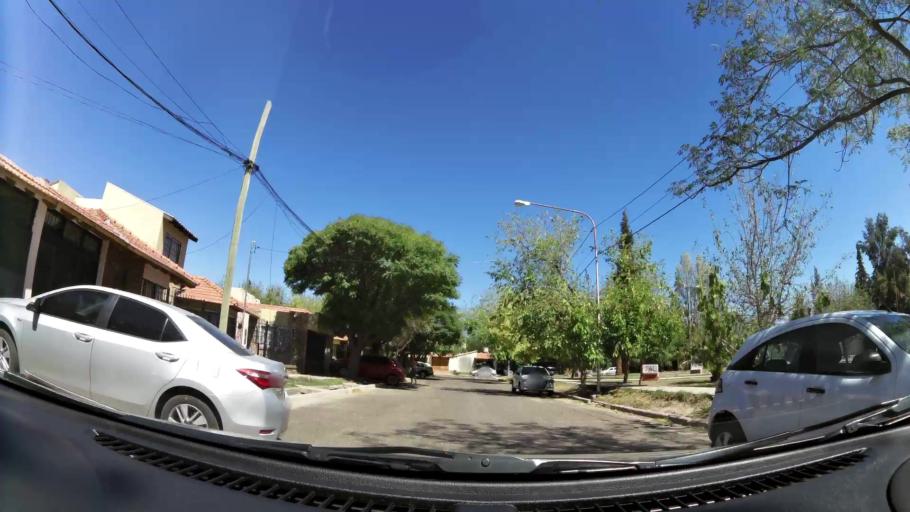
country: AR
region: Mendoza
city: Las Heras
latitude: -32.8571
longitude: -68.8505
